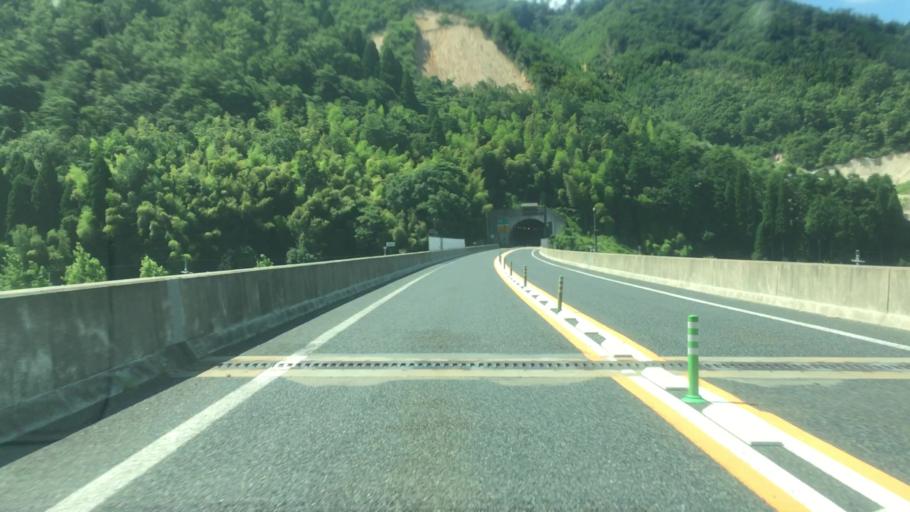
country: JP
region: Tottori
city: Tottori
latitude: 35.3095
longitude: 134.1872
